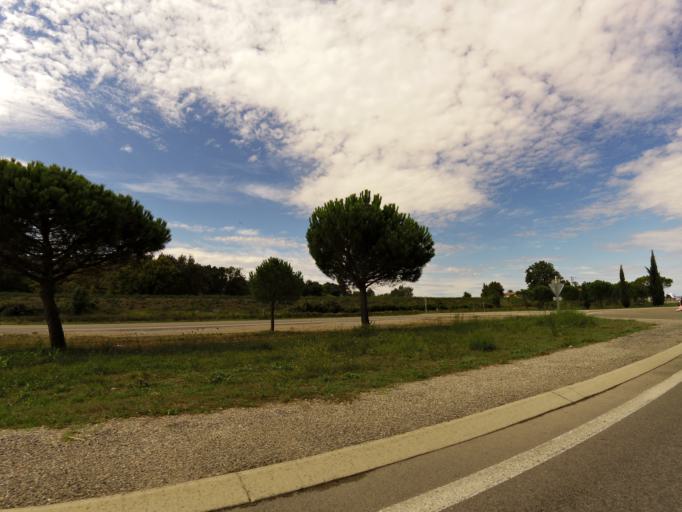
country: FR
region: Languedoc-Roussillon
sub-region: Departement de l'Herault
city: Marsillargues
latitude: 43.6409
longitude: 4.1947
